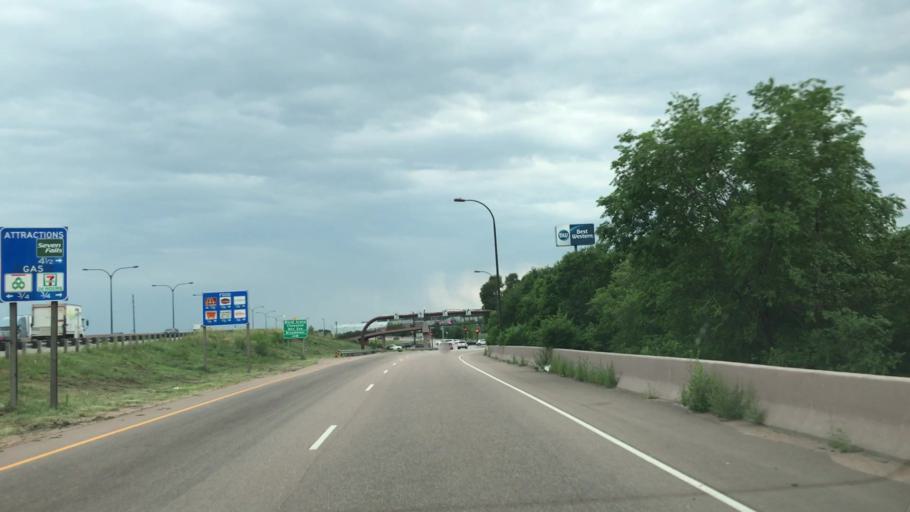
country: US
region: Colorado
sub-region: El Paso County
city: Stratmoor
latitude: 38.7981
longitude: -104.7989
